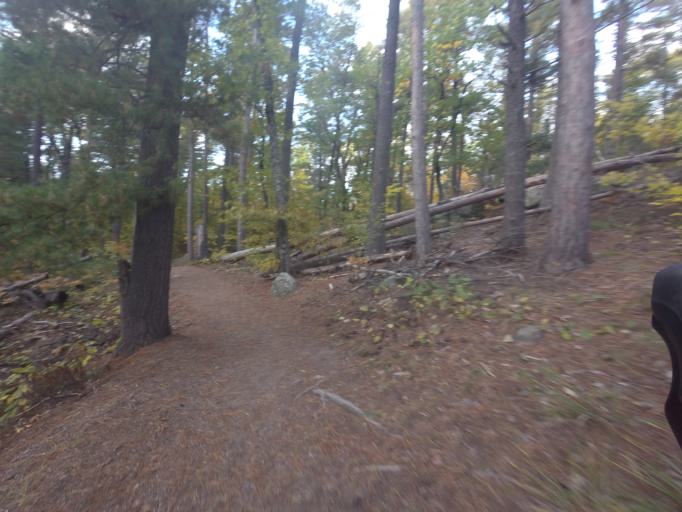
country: CA
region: Ontario
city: Deep River
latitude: 45.8857
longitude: -77.6364
